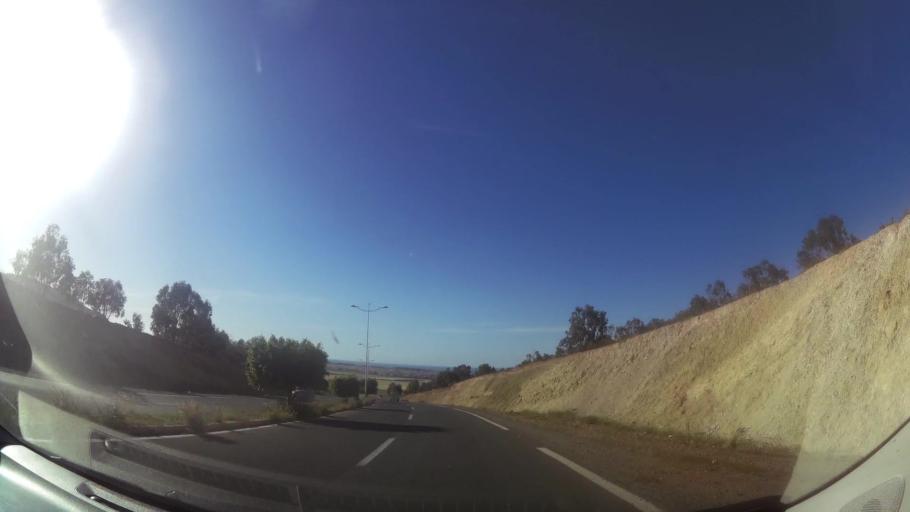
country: MA
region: Oriental
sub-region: Berkane-Taourirt
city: Madagh
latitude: 35.0582
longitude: -2.2217
